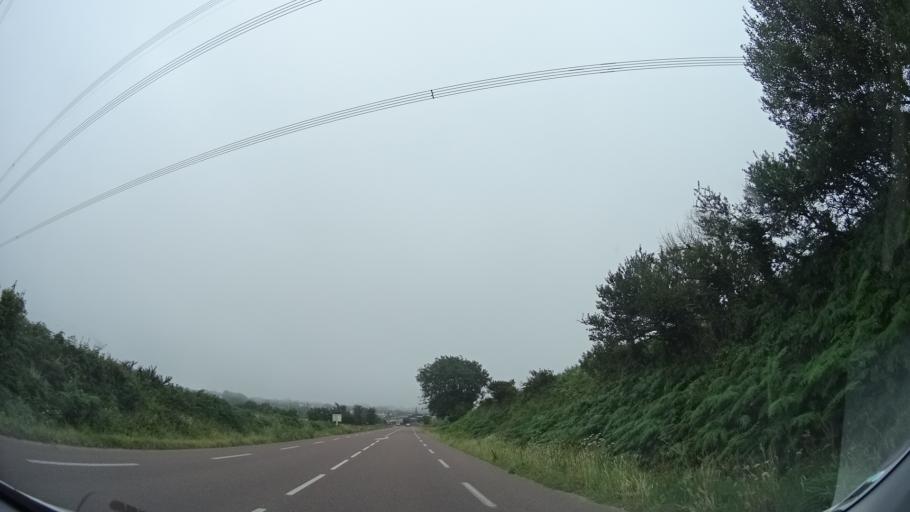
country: FR
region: Lower Normandy
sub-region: Departement de la Manche
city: Les Pieux
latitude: 49.5209
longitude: -1.8159
